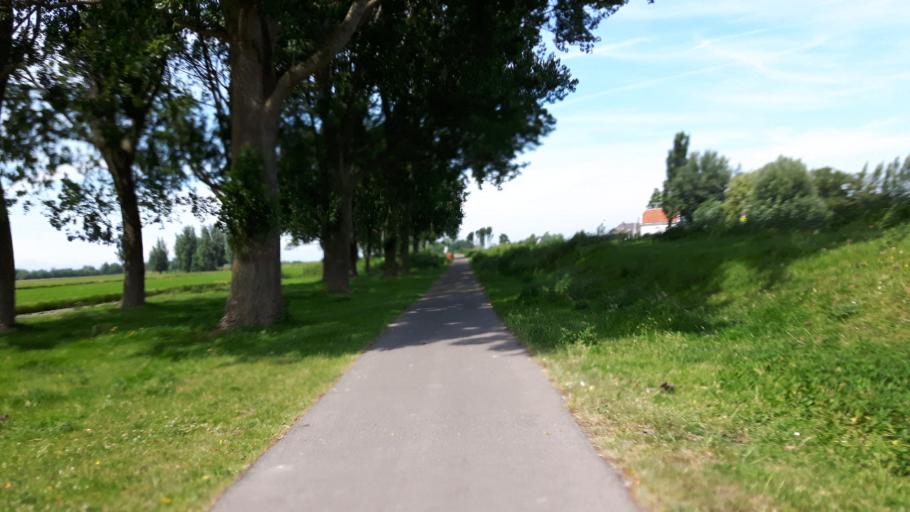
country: NL
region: North Holland
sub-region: Gemeente Aalsmeer
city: Aalsmeer
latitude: 52.2044
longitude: 4.7350
